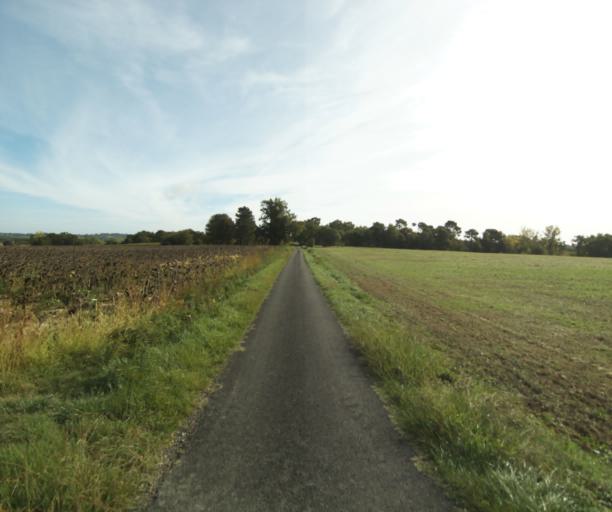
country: FR
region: Midi-Pyrenees
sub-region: Departement du Gers
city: Eauze
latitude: 43.9414
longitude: 0.1013
